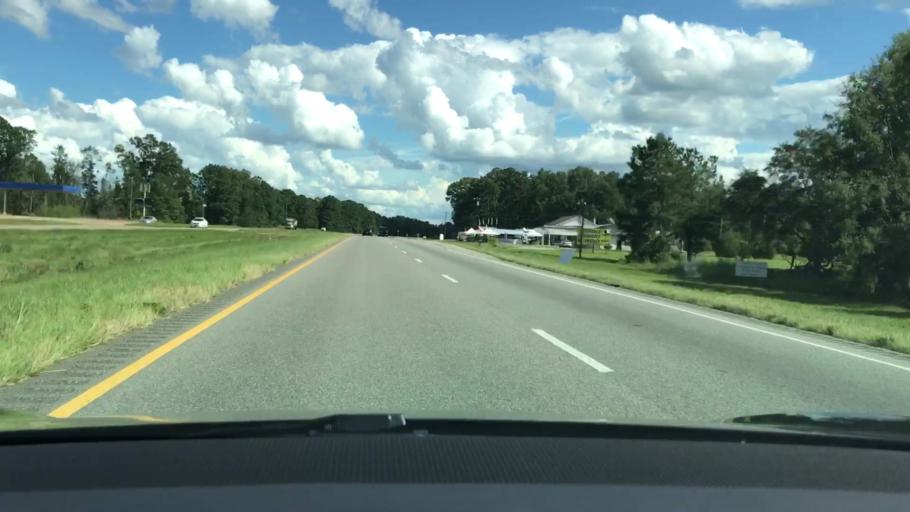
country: US
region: Alabama
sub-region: Montgomery County
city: Taylor
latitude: 32.0462
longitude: -86.0389
